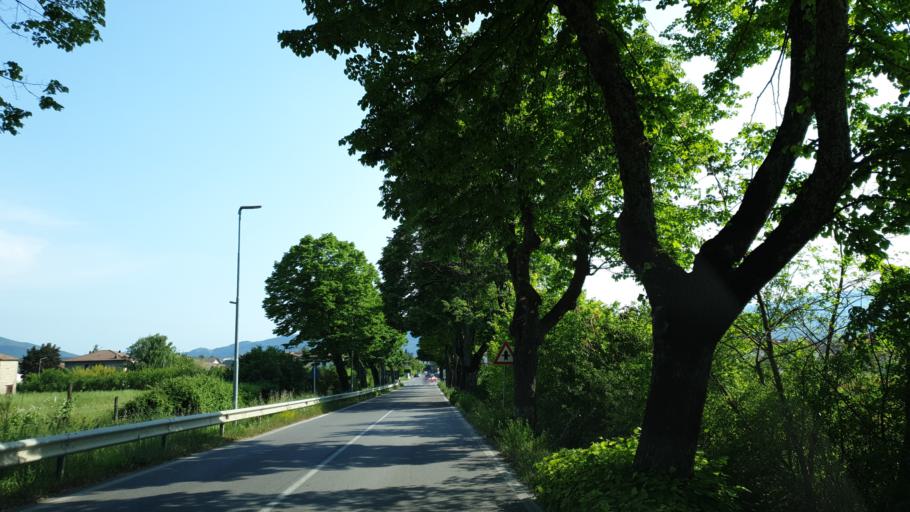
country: IT
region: Tuscany
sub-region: Province of Arezzo
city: Soci
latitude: 43.7414
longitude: 11.8140
